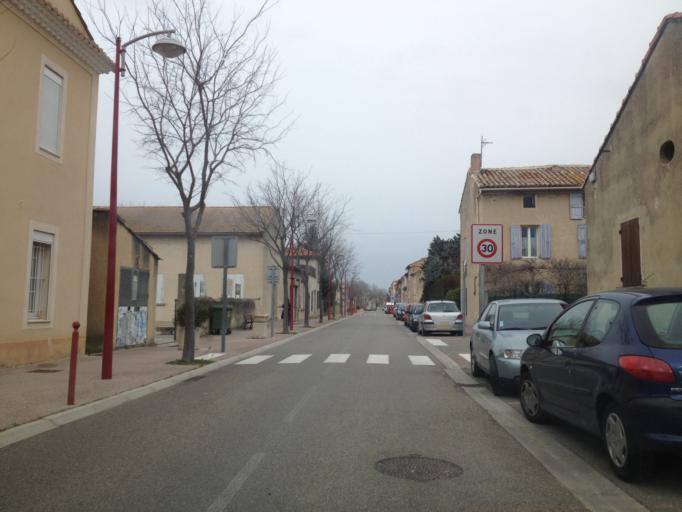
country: FR
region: Provence-Alpes-Cote d'Azur
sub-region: Departement du Vaucluse
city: Jonquieres
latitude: 44.1130
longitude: 4.9009
